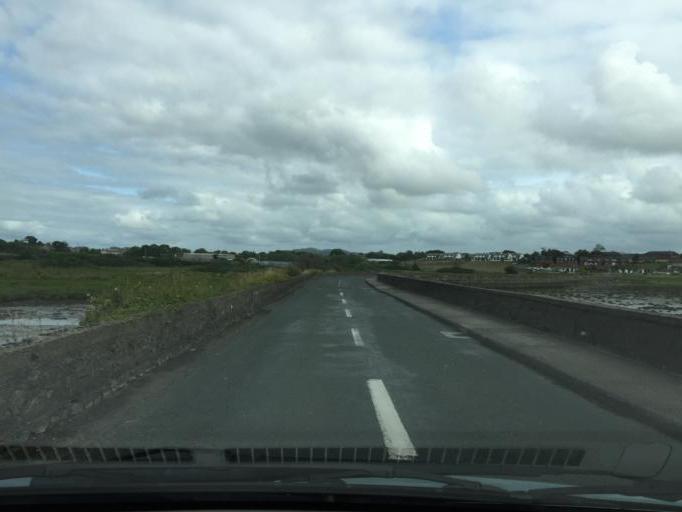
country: IE
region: Connaught
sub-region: Sligo
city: Sligo
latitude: 54.2870
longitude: -8.4797
